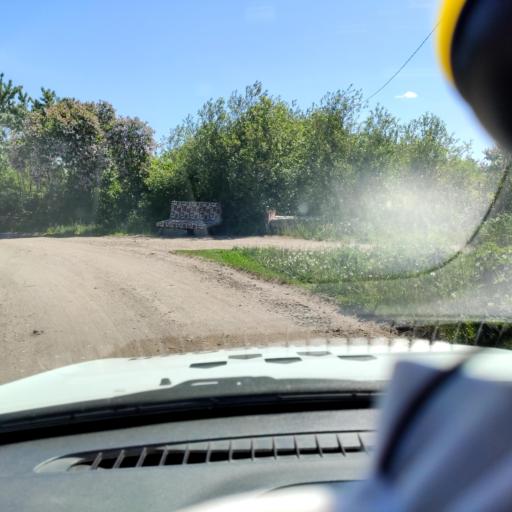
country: RU
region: Samara
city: Tol'yatti
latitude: 53.6093
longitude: 49.4498
